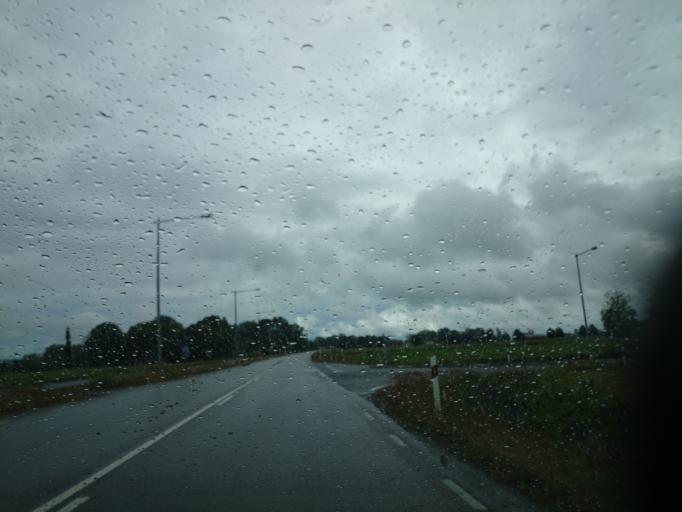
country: SE
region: Joenkoeping
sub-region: Varnamo Kommun
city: Varnamo
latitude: 57.1673
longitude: 14.0334
